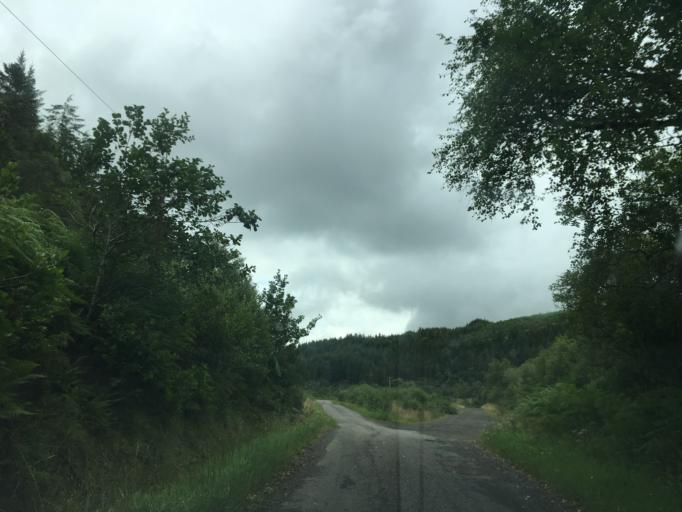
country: GB
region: Scotland
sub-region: Argyll and Bute
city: Oban
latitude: 56.2877
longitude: -5.3090
